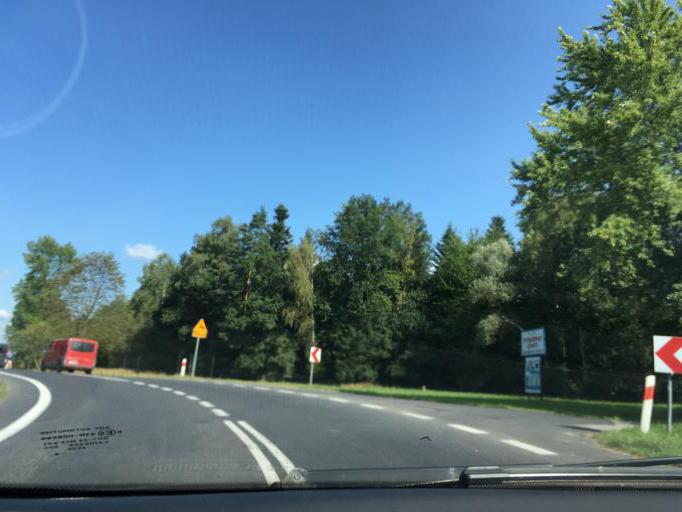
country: PL
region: Subcarpathian Voivodeship
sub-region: Powiat sanocki
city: Zagorz
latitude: 49.5028
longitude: 22.2992
